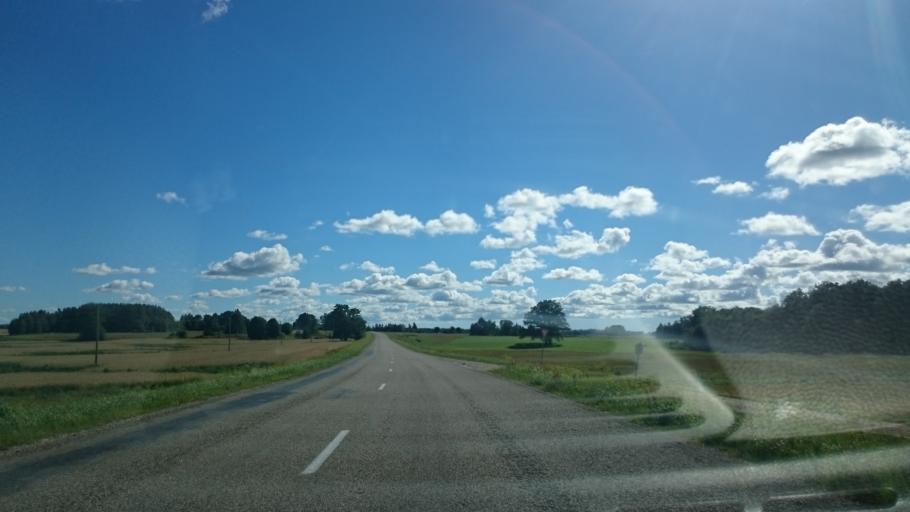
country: LV
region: Aizpute
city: Aizpute
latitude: 56.7703
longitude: 21.6252
